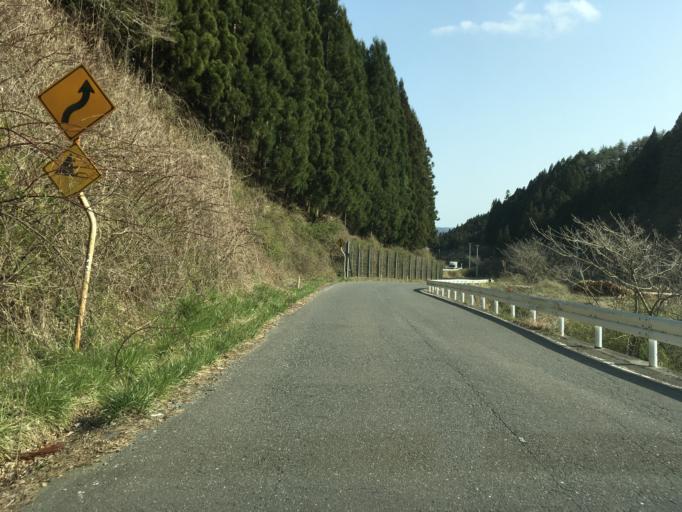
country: JP
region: Iwate
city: Ichinoseki
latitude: 38.8089
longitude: 141.3142
